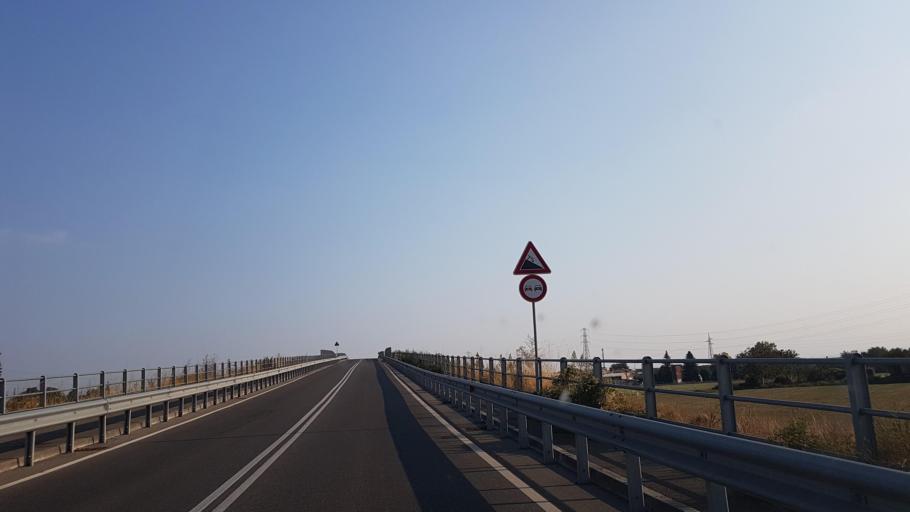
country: IT
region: Emilia-Romagna
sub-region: Provincia di Parma
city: Vicofertile
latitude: 44.7929
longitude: 10.2883
